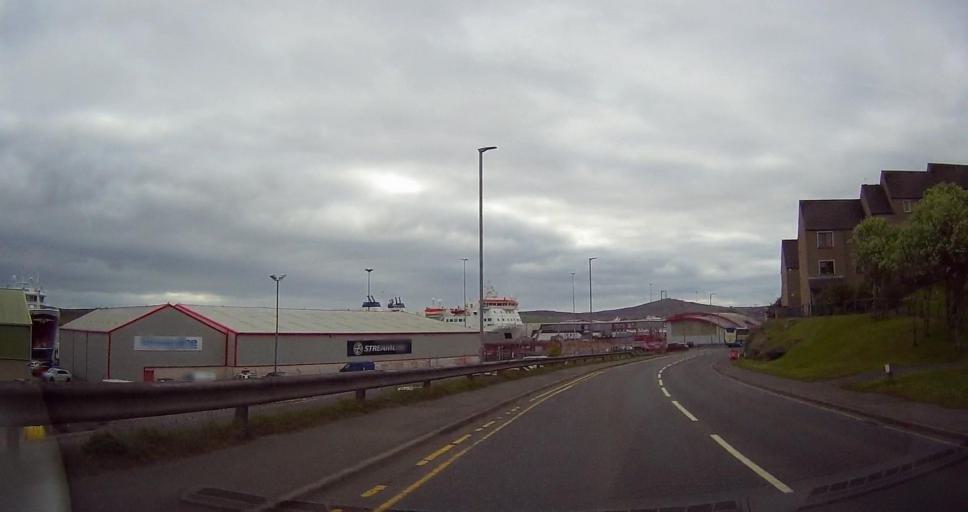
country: GB
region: Scotland
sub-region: Shetland Islands
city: Lerwick
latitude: 60.1640
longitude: -1.1610
